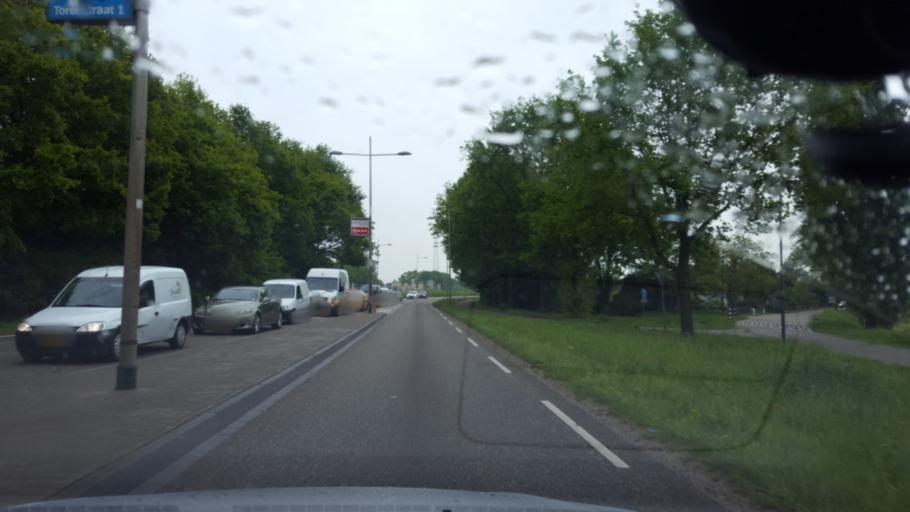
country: NL
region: North Brabant
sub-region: Gemeente Helmond
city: Helmond
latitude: 51.4649
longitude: 5.6630
